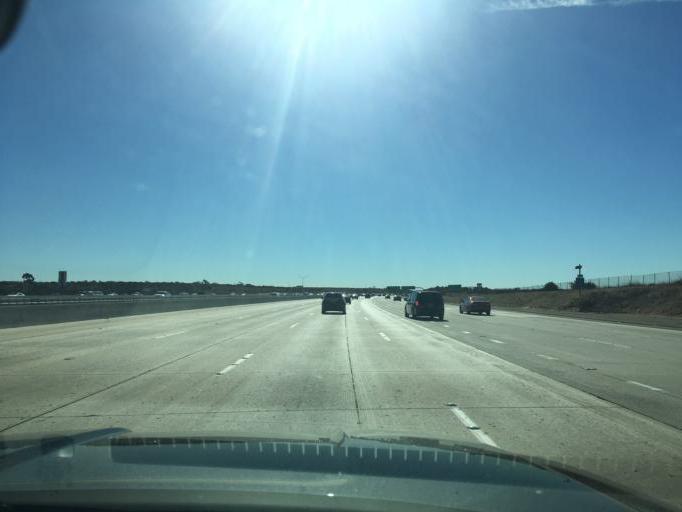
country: US
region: California
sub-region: San Diego County
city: Poway
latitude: 32.8753
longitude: -117.1077
